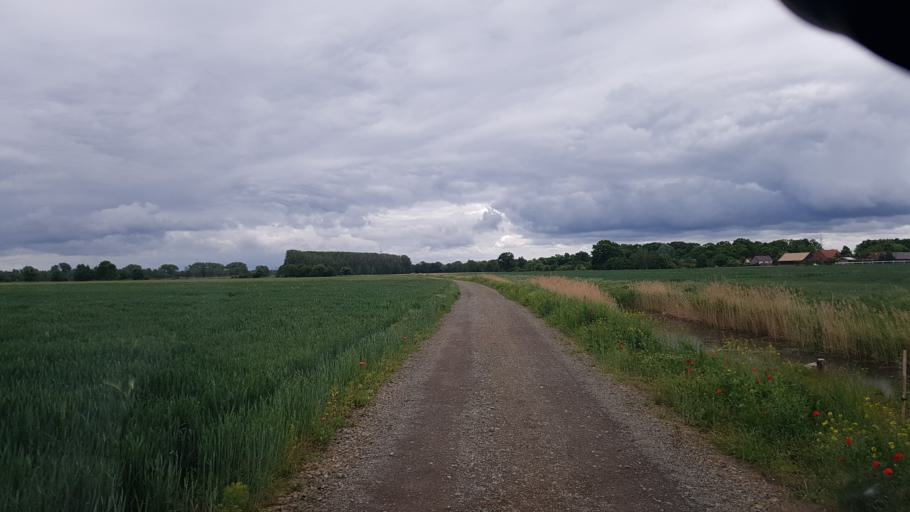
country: DE
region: Brandenburg
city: Doberlug-Kirchhain
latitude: 51.6567
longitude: 13.5468
